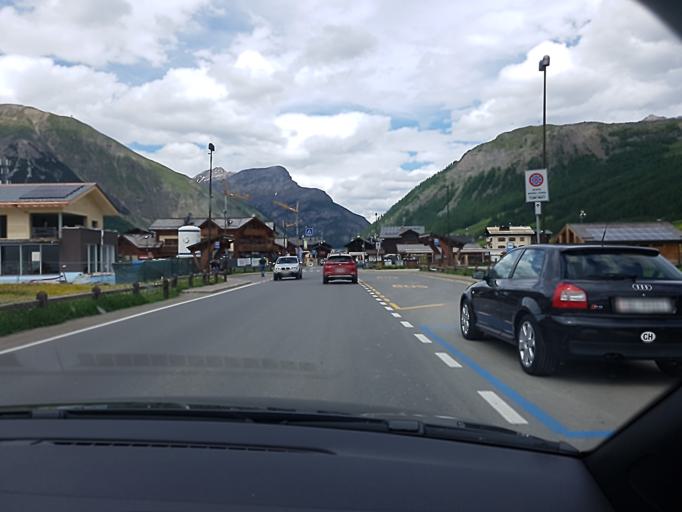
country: IT
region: Lombardy
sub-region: Provincia di Sondrio
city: Livigno
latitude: 46.5362
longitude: 10.1364
